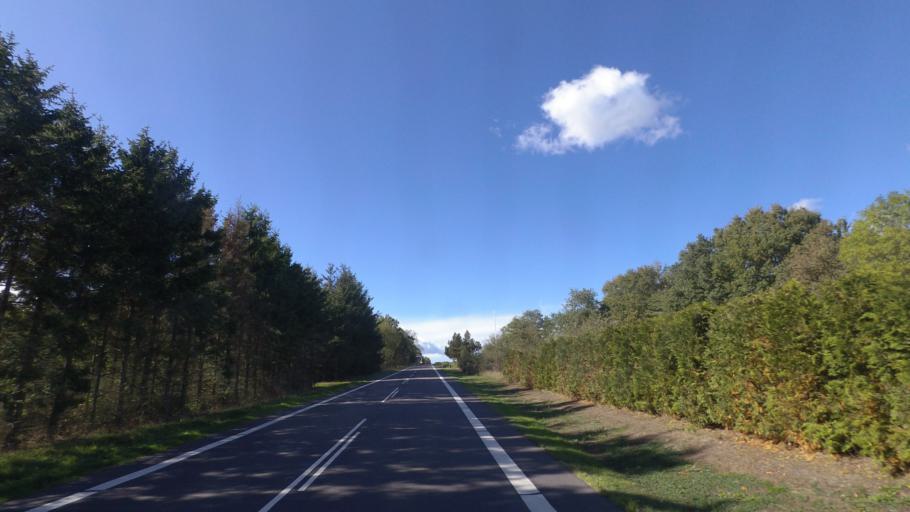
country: DK
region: Capital Region
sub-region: Bornholm Kommune
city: Akirkeby
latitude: 55.0654
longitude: 15.0115
